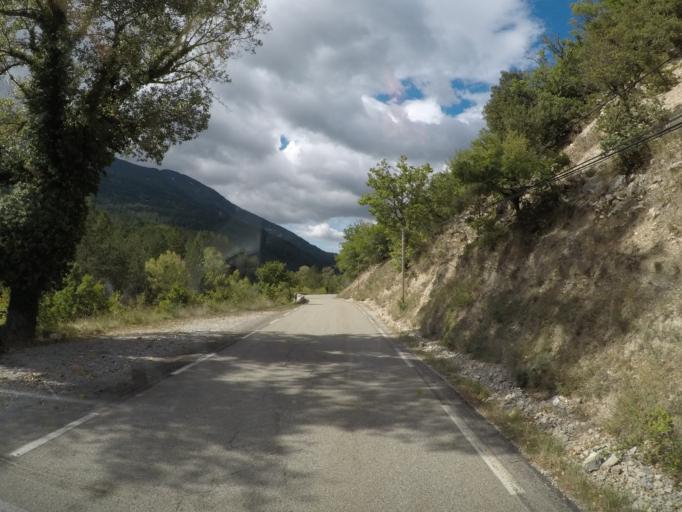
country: FR
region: Rhone-Alpes
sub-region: Departement de la Drome
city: Buis-les-Baronnies
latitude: 44.1935
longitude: 5.3284
